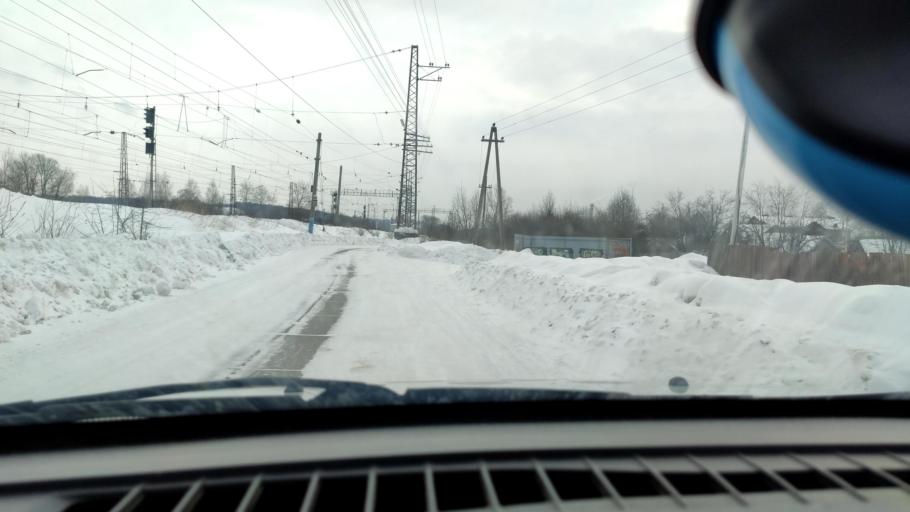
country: RU
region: Perm
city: Overyata
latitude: 58.0829
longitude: 55.8708
